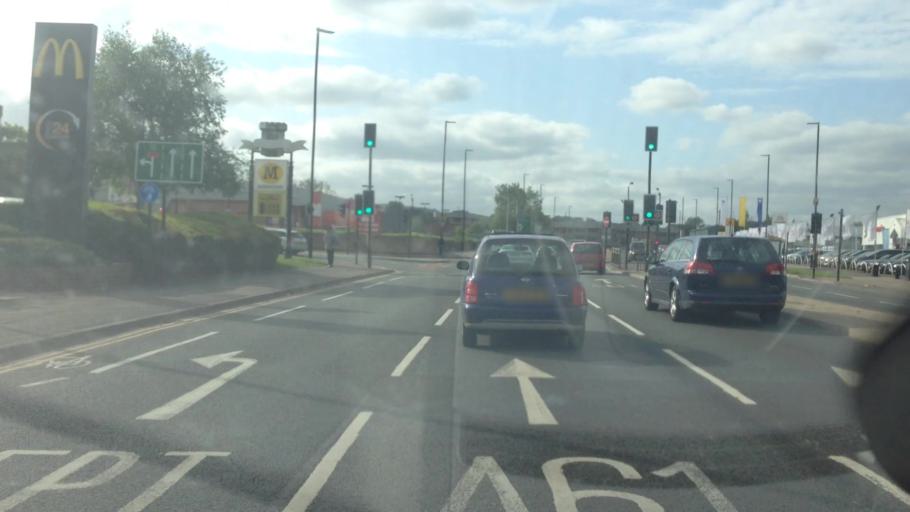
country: GB
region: England
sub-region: Sheffield
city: Sheffield
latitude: 53.4023
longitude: -1.4925
